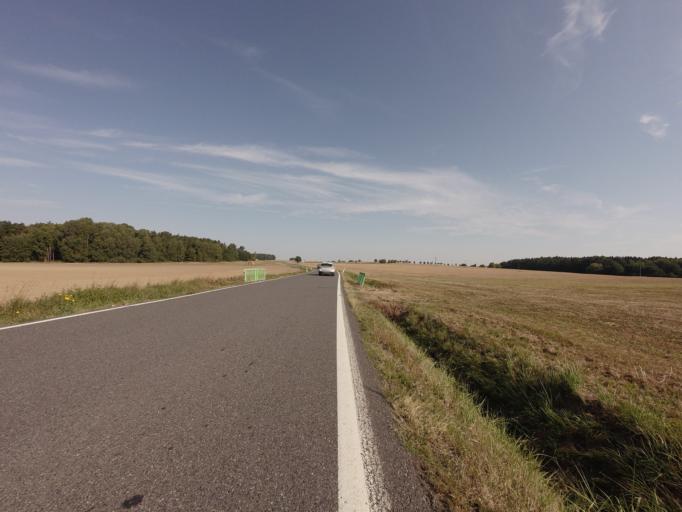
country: CZ
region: Jihocesky
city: Bernartice
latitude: 49.3150
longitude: 14.3725
